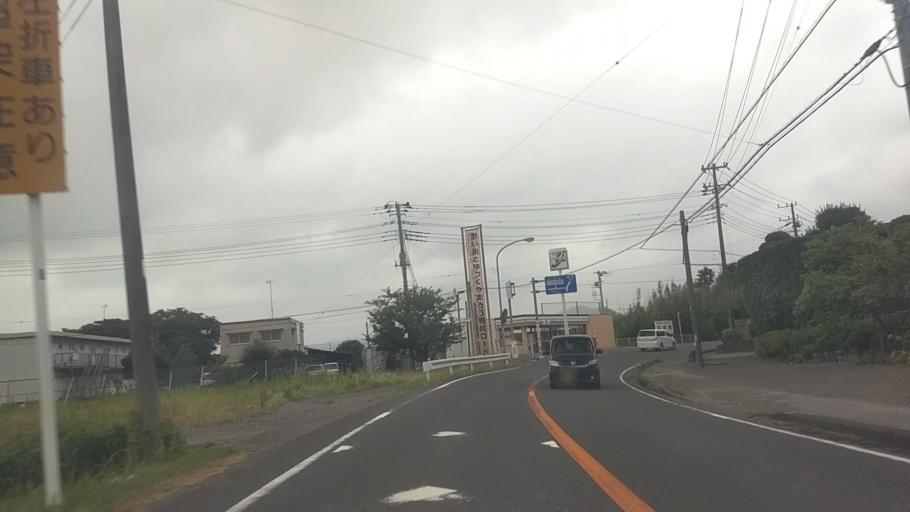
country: JP
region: Chiba
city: Kawaguchi
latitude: 35.1109
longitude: 140.0818
